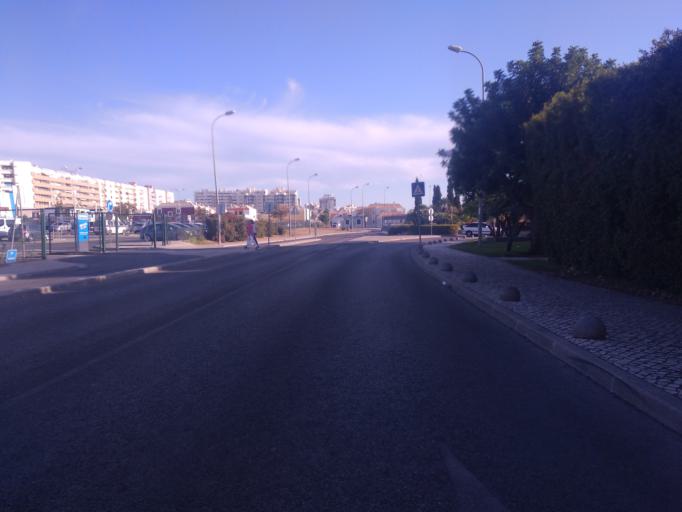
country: PT
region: Faro
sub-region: Faro
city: Faro
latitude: 37.0288
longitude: -7.9433
